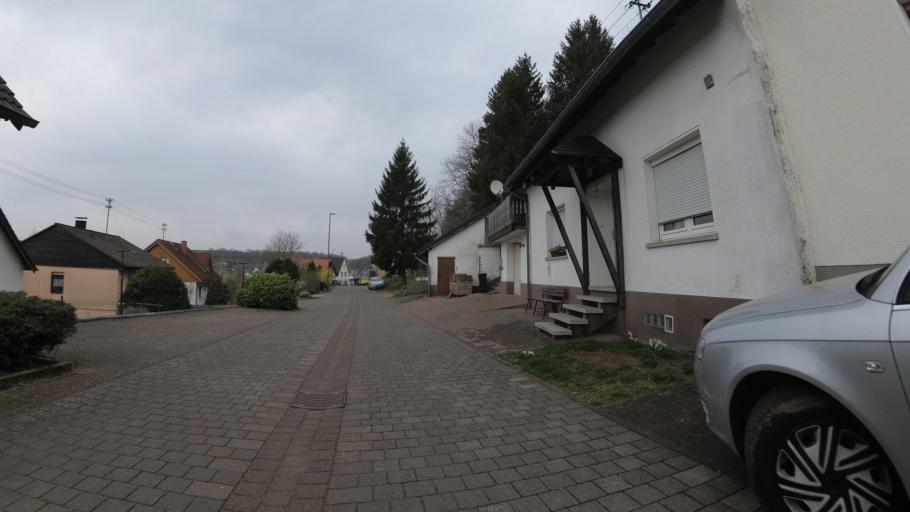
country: DE
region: Rheinland-Pfalz
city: Gimbweiler
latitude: 49.5818
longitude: 7.1922
